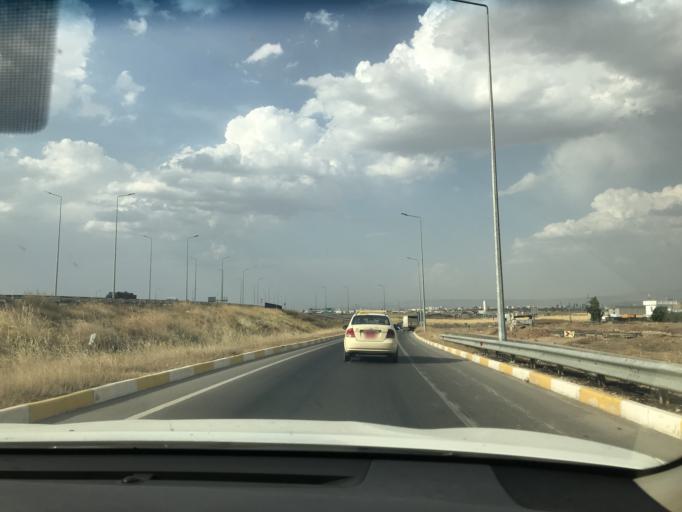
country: IQ
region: Arbil
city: Erbil
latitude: 36.2074
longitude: 43.9538
